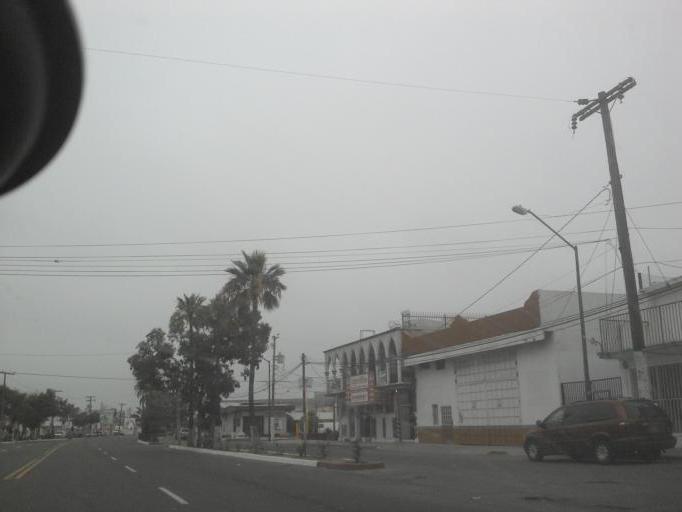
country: US
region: California
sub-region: San Diego County
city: Imperial Beach
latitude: 32.5291
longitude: -117.1201
